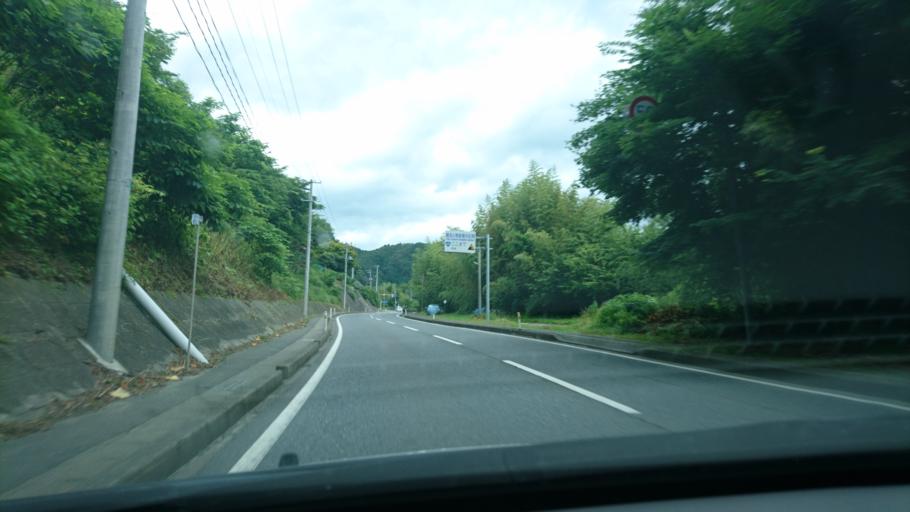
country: JP
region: Iwate
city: Kamaishi
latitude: 39.2041
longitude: 141.8646
